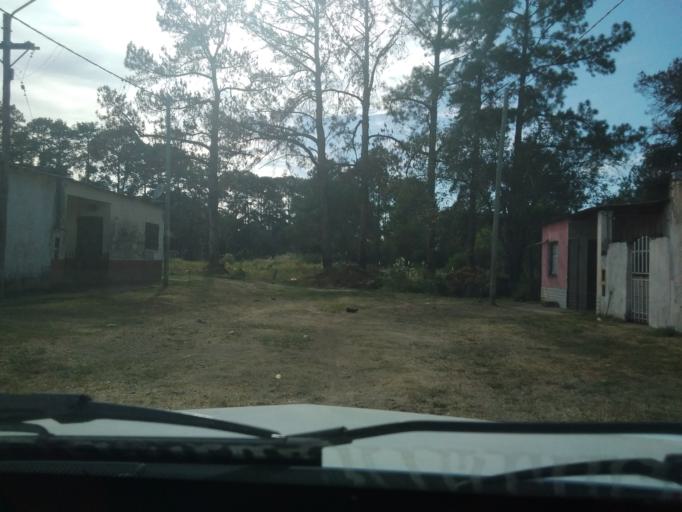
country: AR
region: Corrientes
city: Corrientes
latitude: -27.5077
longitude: -58.8045
